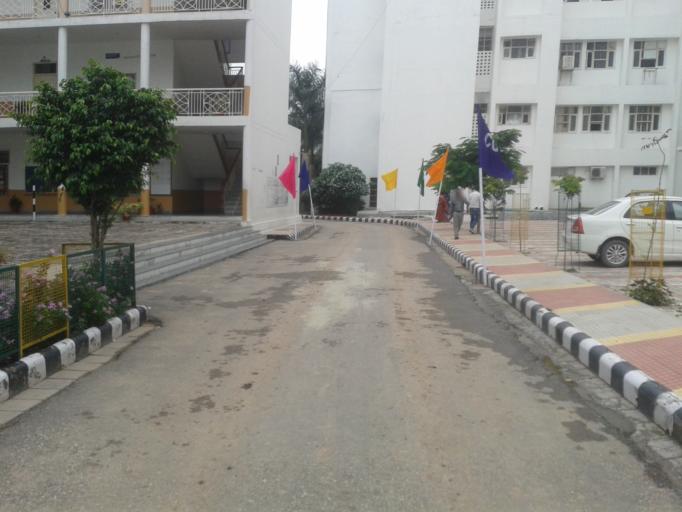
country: IN
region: Punjab
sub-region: Ajitgarh
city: Mohali
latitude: 30.6864
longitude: 76.6660
